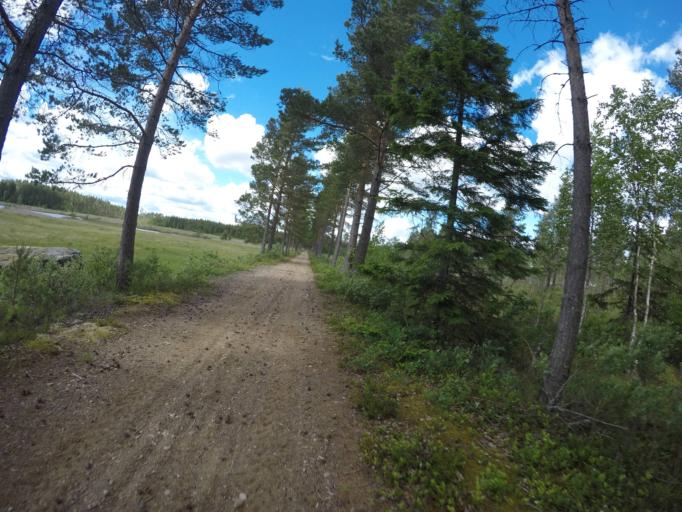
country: SE
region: Vaermland
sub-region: Filipstads Kommun
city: Lesjofors
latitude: 60.1376
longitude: 14.2995
